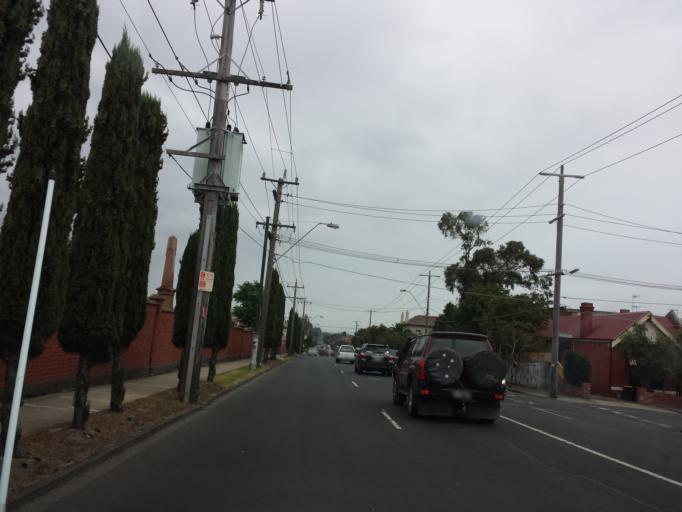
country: AU
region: Victoria
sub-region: Port Phillip
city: St Kilda East
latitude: -37.8611
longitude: 145.0010
